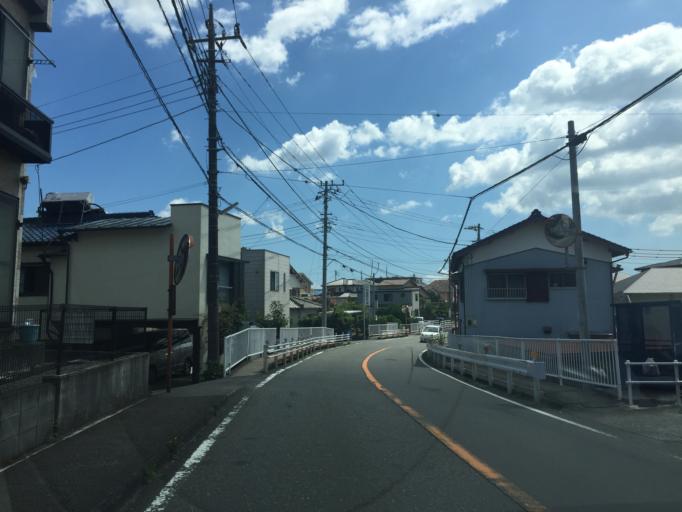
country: JP
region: Shizuoka
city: Mishima
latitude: 35.1845
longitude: 138.9065
